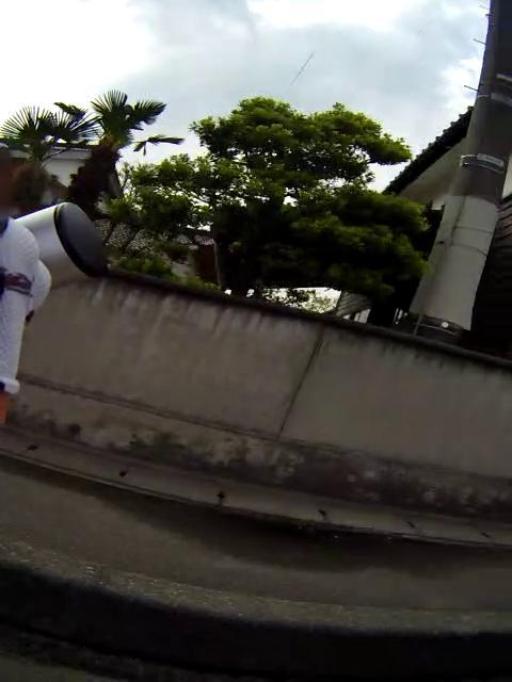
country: JP
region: Toyama
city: Takaoka
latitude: 36.7128
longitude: 136.9898
